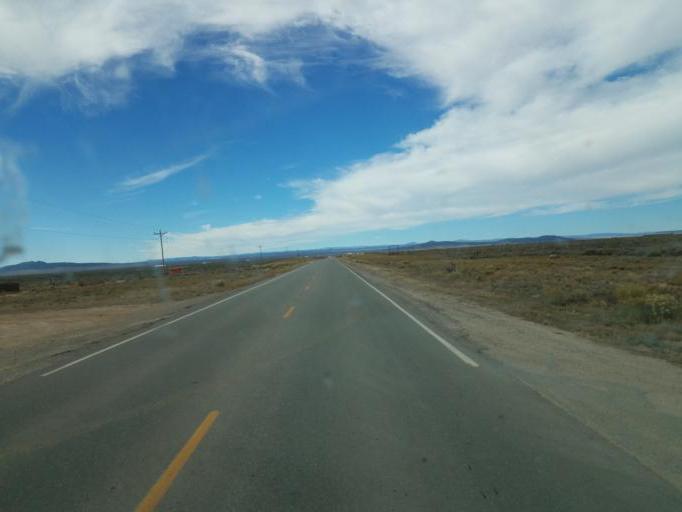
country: US
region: New Mexico
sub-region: Taos County
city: Taos
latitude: 36.4611
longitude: -105.6408
